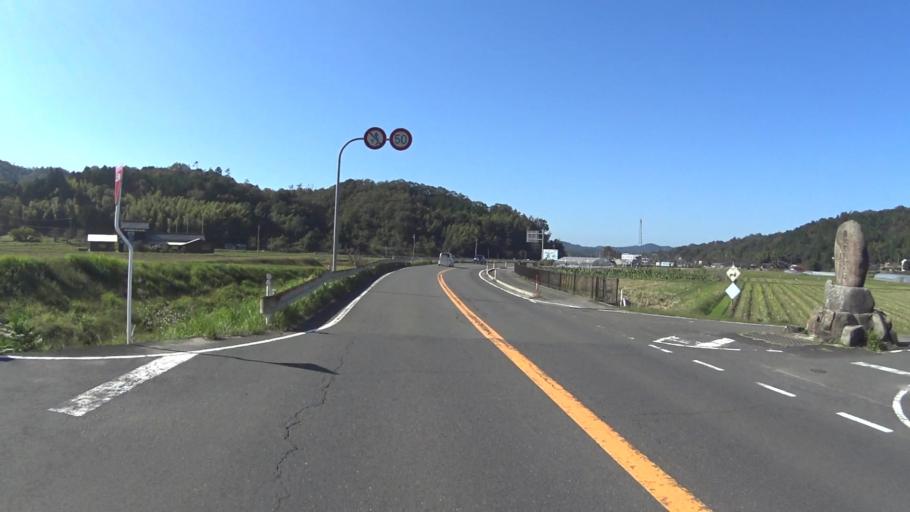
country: JP
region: Hyogo
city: Toyooka
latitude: 35.5743
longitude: 134.9766
